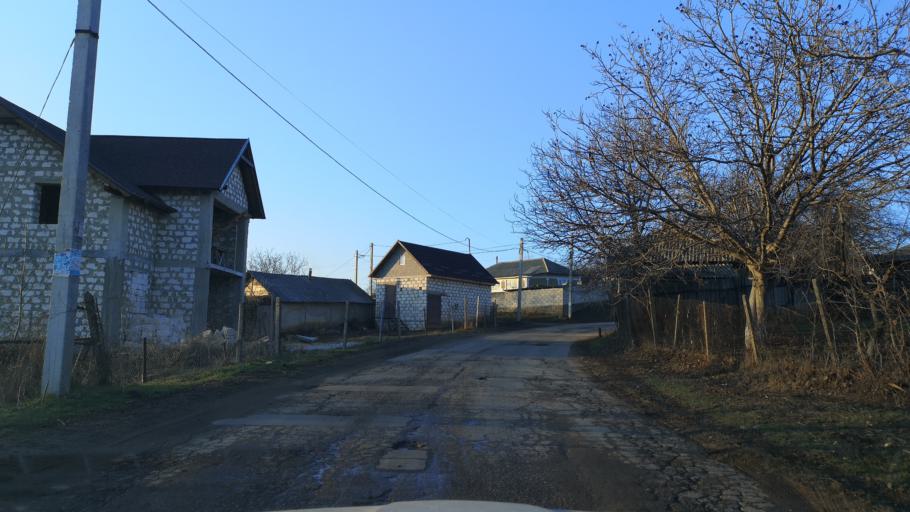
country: MD
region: Orhei
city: Orhei
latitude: 47.3553
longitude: 28.6901
